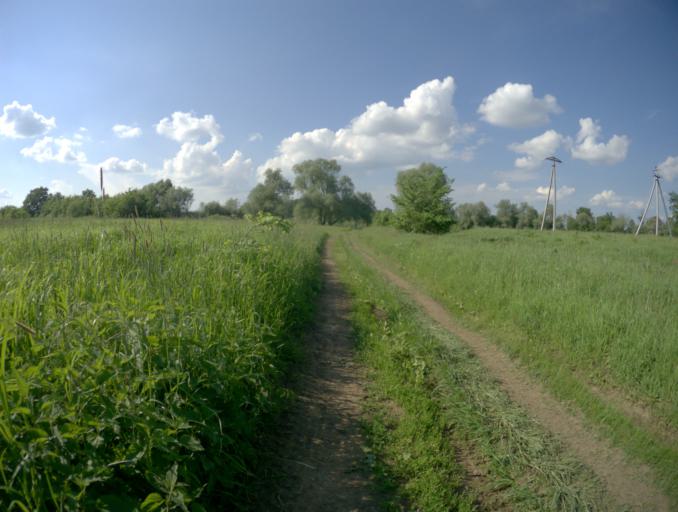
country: RU
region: Vladimir
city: Raduzhnyy
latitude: 56.0387
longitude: 40.2907
